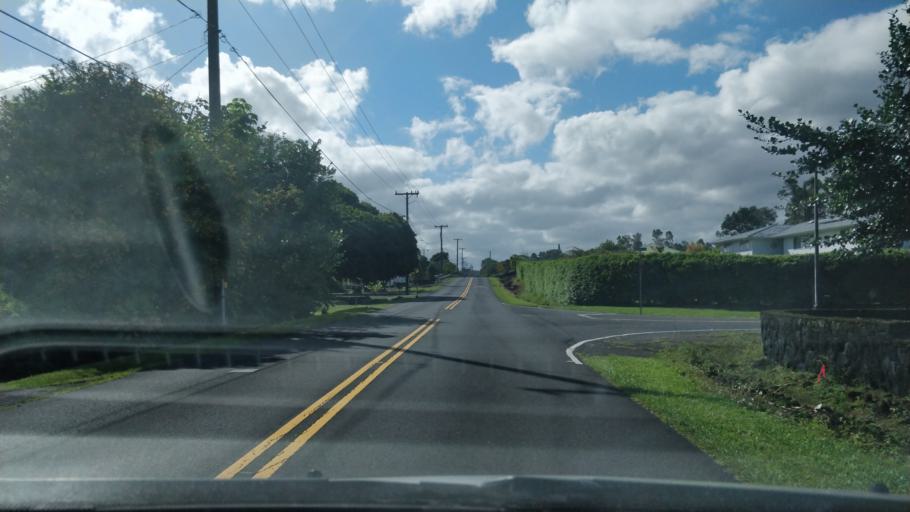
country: US
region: Hawaii
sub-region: Hawaii County
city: Hilo
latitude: 19.6799
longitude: -155.1064
